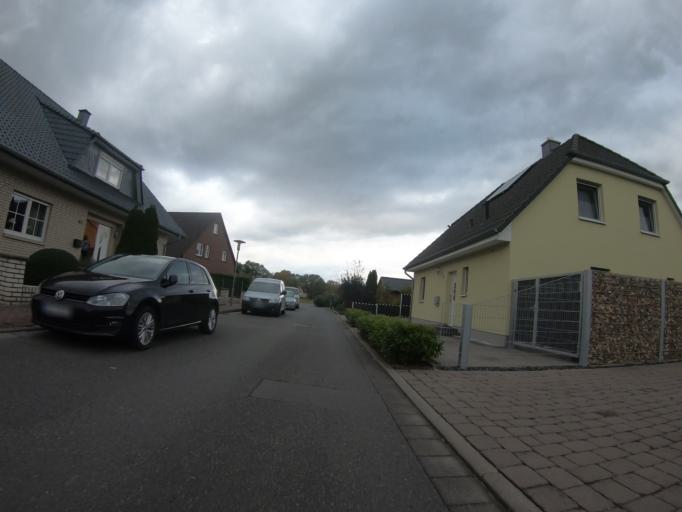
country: DE
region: Lower Saxony
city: Isenbuttel
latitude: 52.4418
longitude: 10.5740
